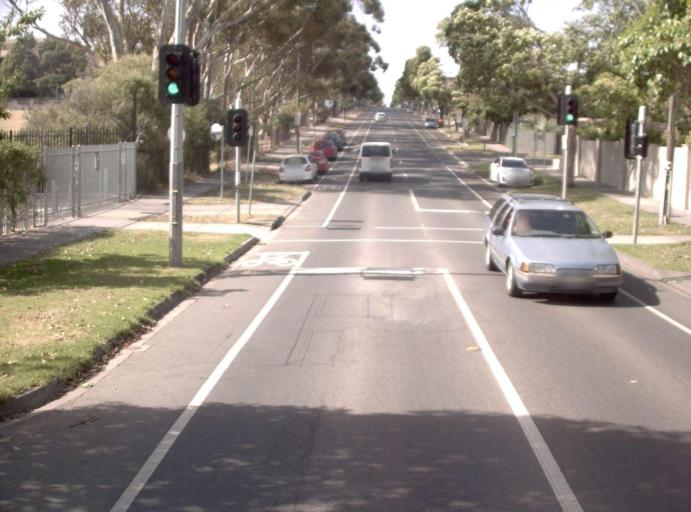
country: AU
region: Victoria
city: Glenferrie
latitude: -37.8423
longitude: 145.0455
